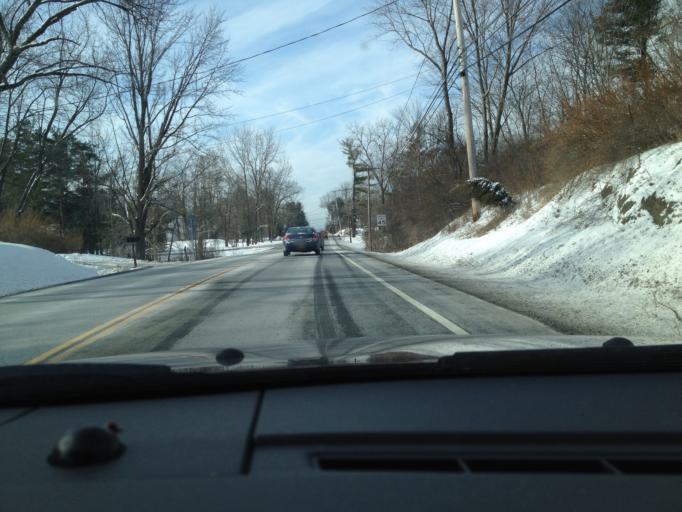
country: US
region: New York
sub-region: Rensselaer County
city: Wynantskill
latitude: 42.6532
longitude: -73.6808
